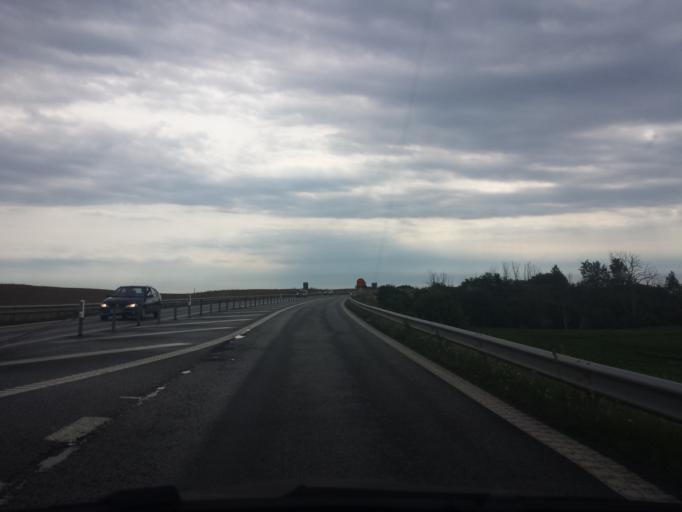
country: SE
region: Skane
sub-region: Ystads Kommun
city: Ystad
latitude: 55.4464
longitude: 13.7755
